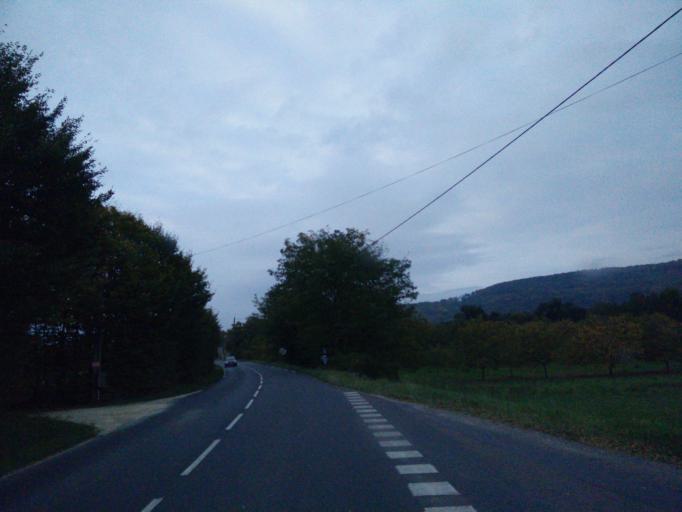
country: FR
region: Aquitaine
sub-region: Departement de la Dordogne
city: Carsac-Aillac
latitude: 44.8326
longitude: 1.2752
